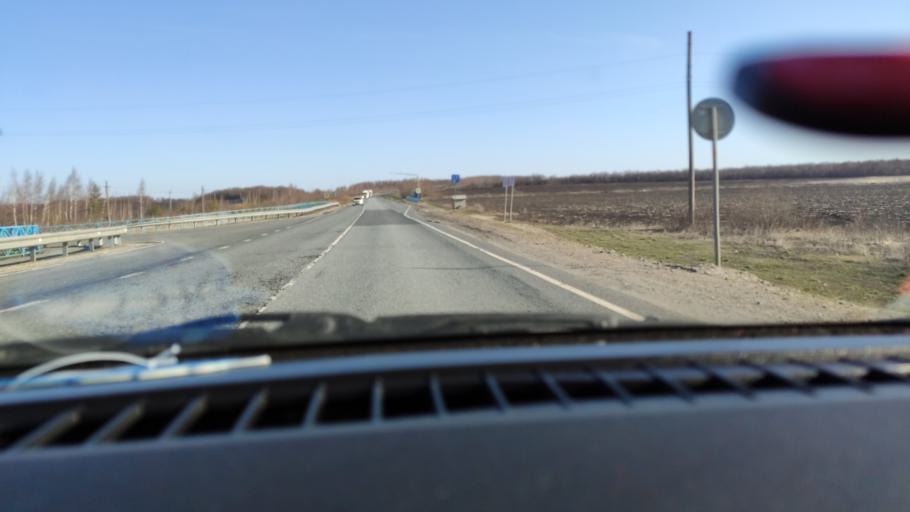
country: RU
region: Samara
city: Syzran'
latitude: 52.9699
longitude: 48.3082
